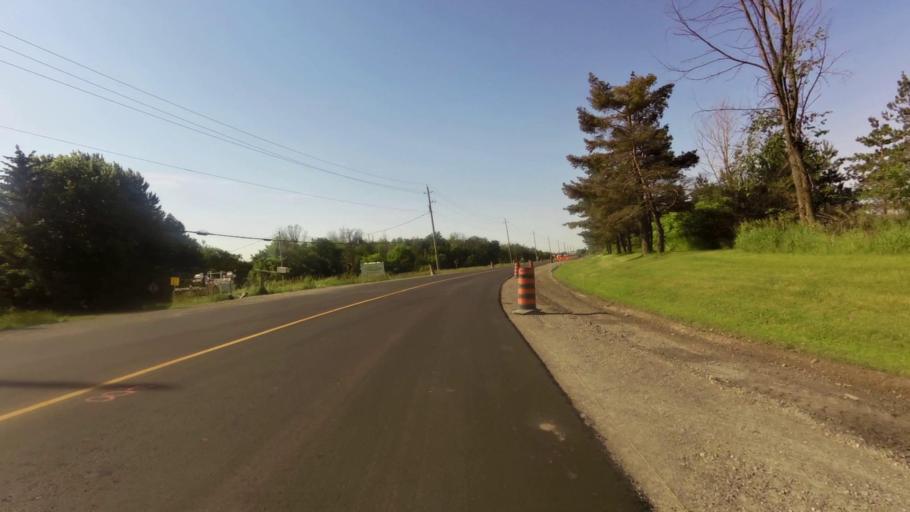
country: CA
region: Ontario
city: Ottawa
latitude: 45.2128
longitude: -75.5682
